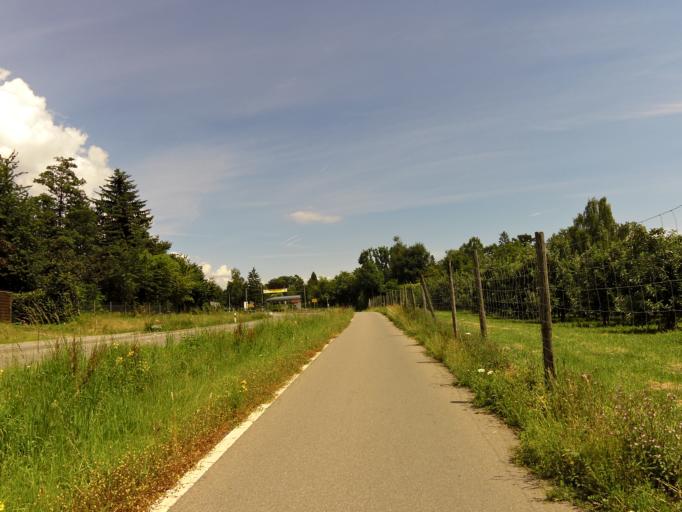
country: DE
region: Baden-Wuerttemberg
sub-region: Tuebingen Region
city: Immenstaad am Bodensee
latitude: 47.6700
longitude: 9.4017
